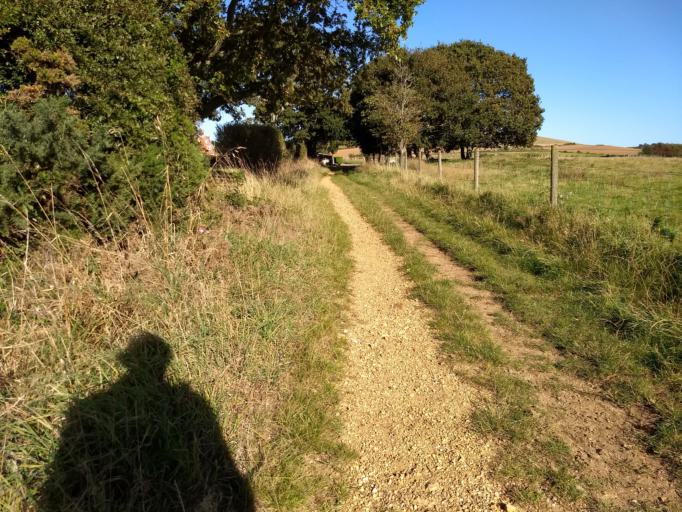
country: GB
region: England
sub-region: Isle of Wight
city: Newport
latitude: 50.6464
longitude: -1.2915
